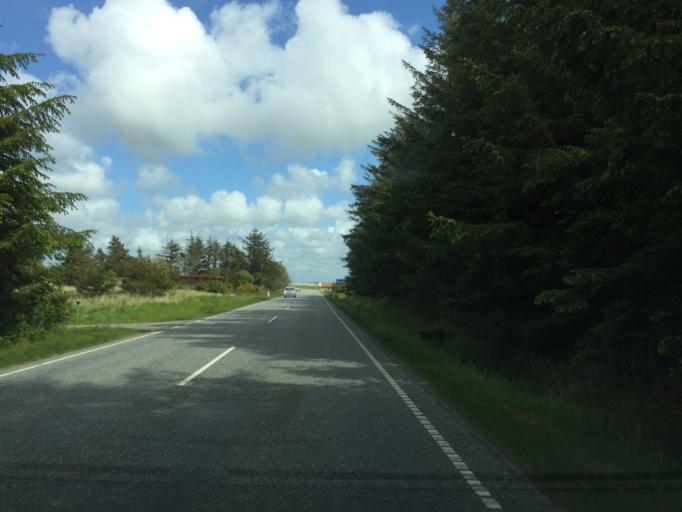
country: DK
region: Central Jutland
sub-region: Holstebro Kommune
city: Ulfborg
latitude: 56.3201
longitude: 8.1353
